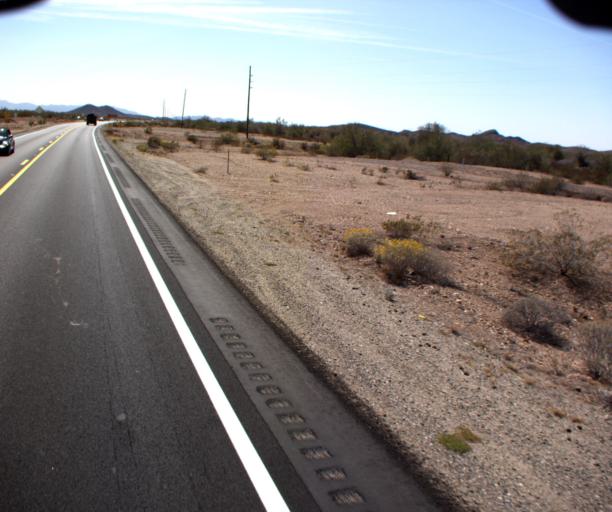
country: US
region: Arizona
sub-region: Yuma County
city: Wellton
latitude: 32.9642
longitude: -114.2923
